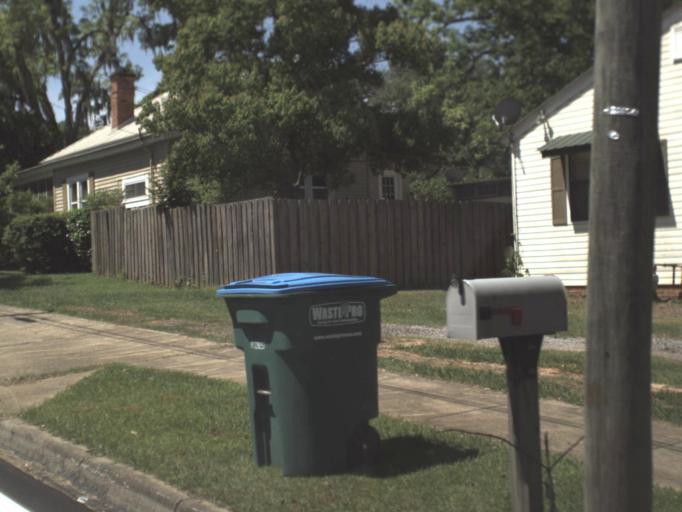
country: US
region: Florida
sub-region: Jackson County
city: Marianna
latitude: 30.7803
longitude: -85.2267
